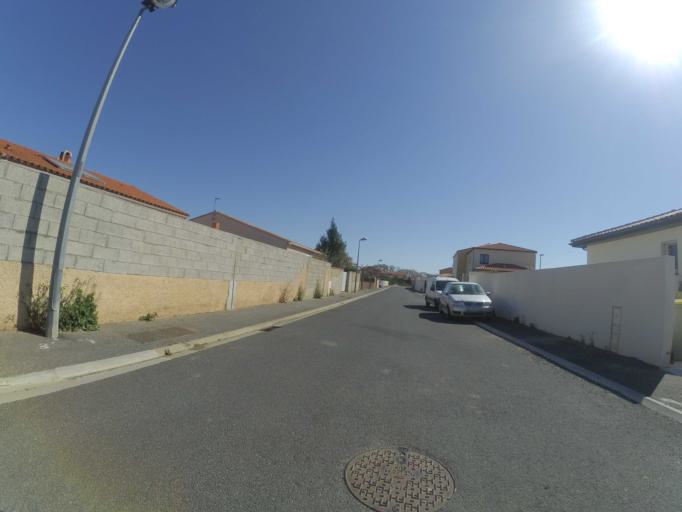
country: FR
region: Languedoc-Roussillon
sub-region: Departement des Pyrenees-Orientales
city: Corneilla-la-Riviere
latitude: 42.6827
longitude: 2.7194
